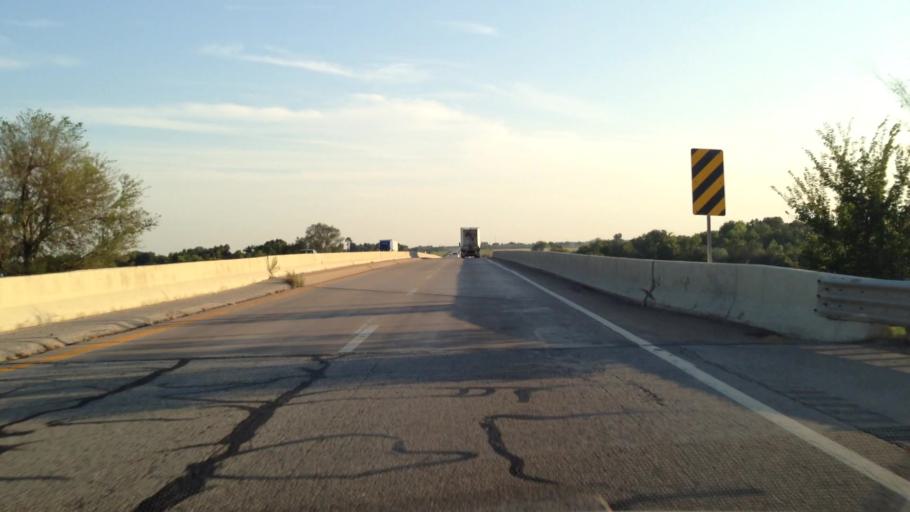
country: US
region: Oklahoma
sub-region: Ottawa County
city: Miami
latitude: 36.8151
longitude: -94.8738
